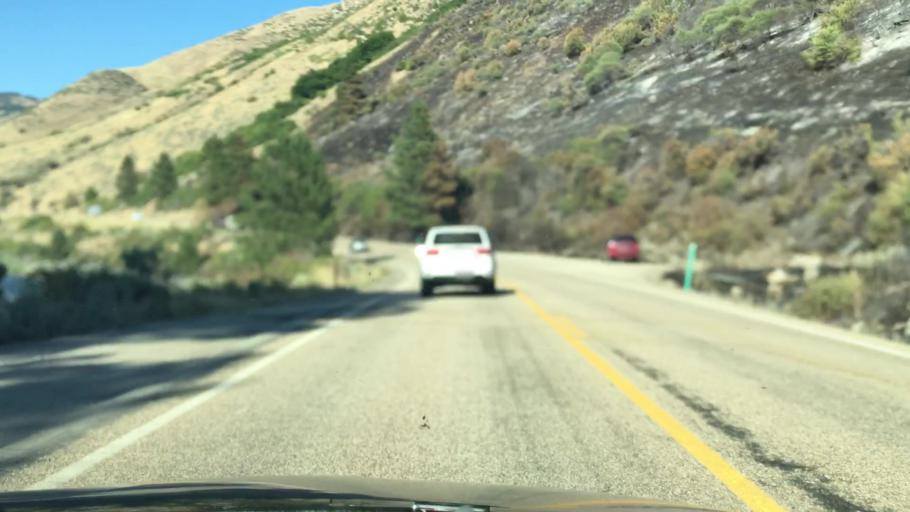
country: US
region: Idaho
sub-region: Gem County
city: Emmett
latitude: 44.0144
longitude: -116.1559
